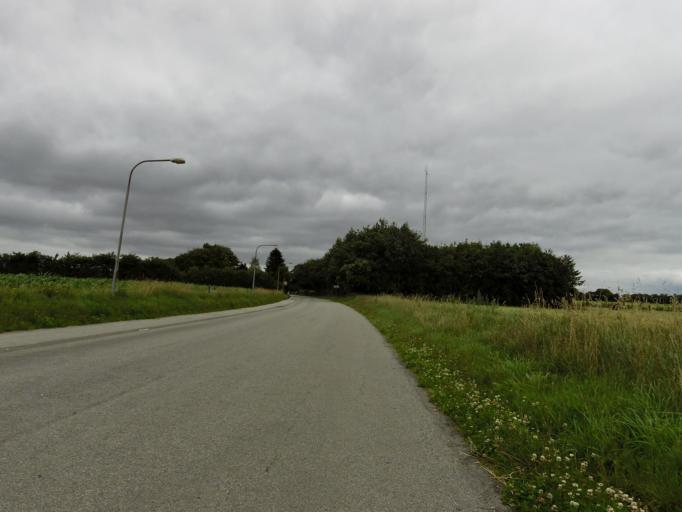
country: DK
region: South Denmark
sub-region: Haderslev Kommune
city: Vojens
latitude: 55.2687
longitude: 9.1777
